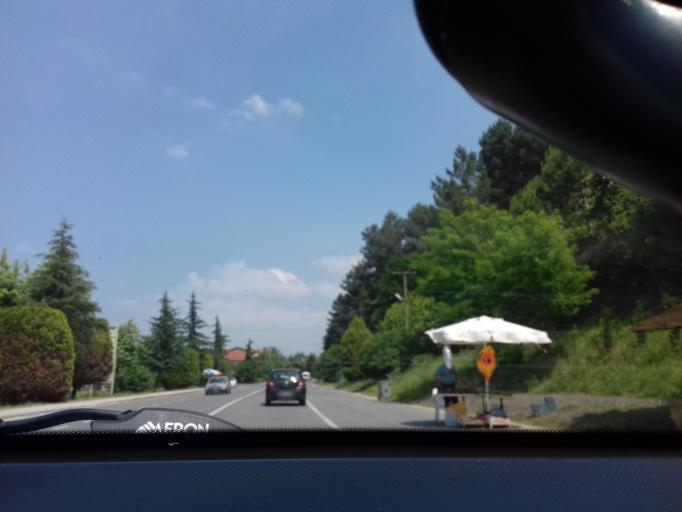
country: TR
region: Sakarya
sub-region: Merkez
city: Sapanca
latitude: 40.6910
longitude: 30.2257
